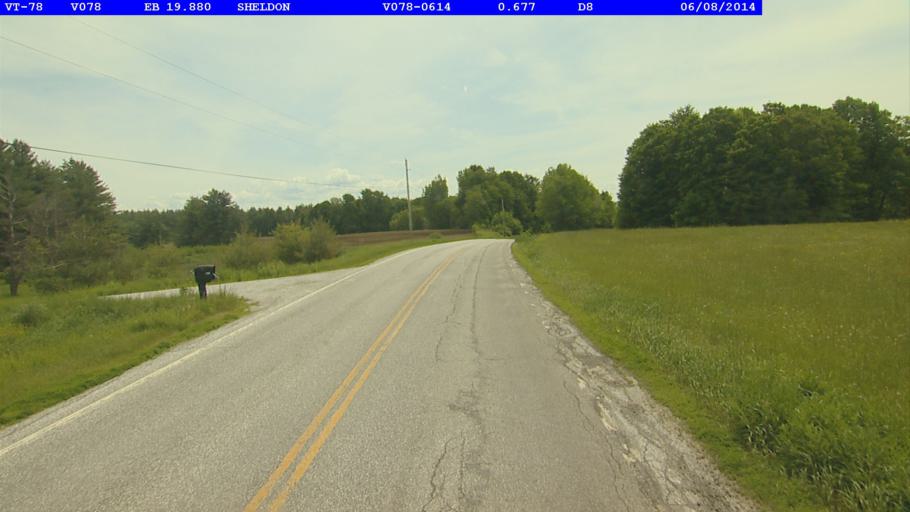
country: US
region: Vermont
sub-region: Franklin County
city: Enosburg Falls
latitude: 44.9166
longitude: -72.9602
